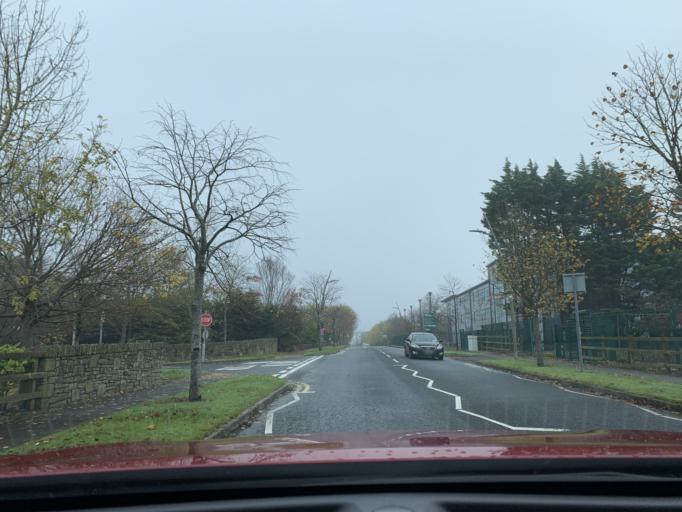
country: IE
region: Connaught
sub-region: Sligo
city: Sligo
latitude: 54.2771
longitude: -8.4948
